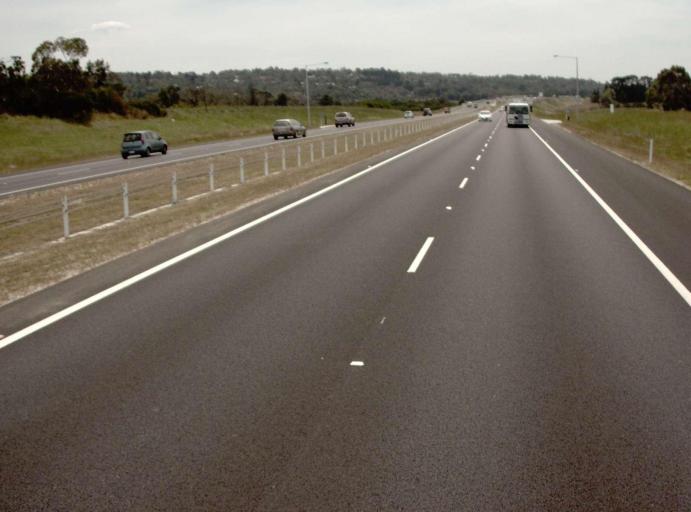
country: AU
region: Victoria
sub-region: Mornington Peninsula
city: Moorooduc
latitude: -38.2157
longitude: 145.1295
